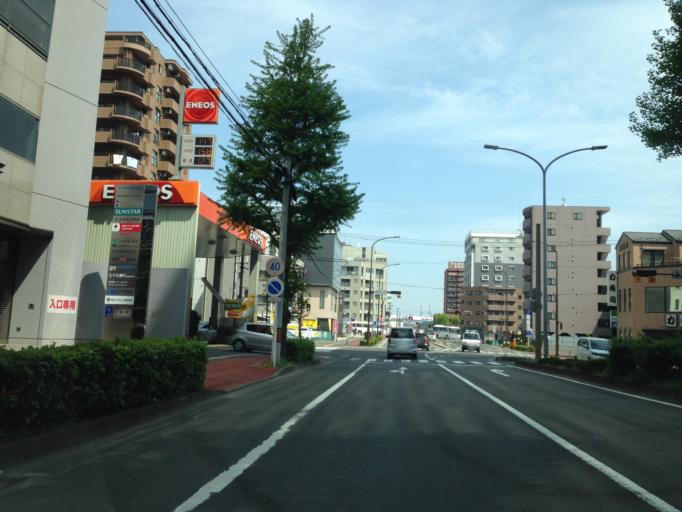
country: JP
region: Miyagi
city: Sendai-shi
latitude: 38.2614
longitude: 140.8864
